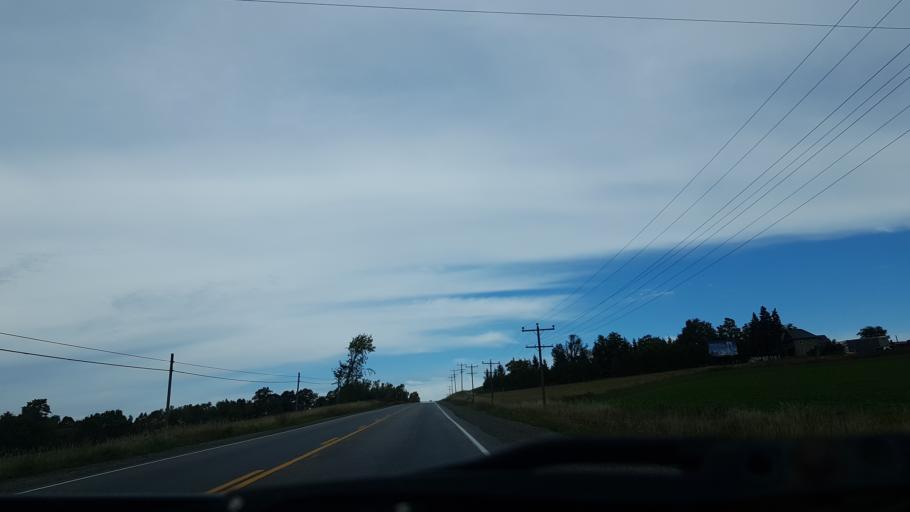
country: CA
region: Ontario
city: Wasaga Beach
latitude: 44.3546
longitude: -80.0820
